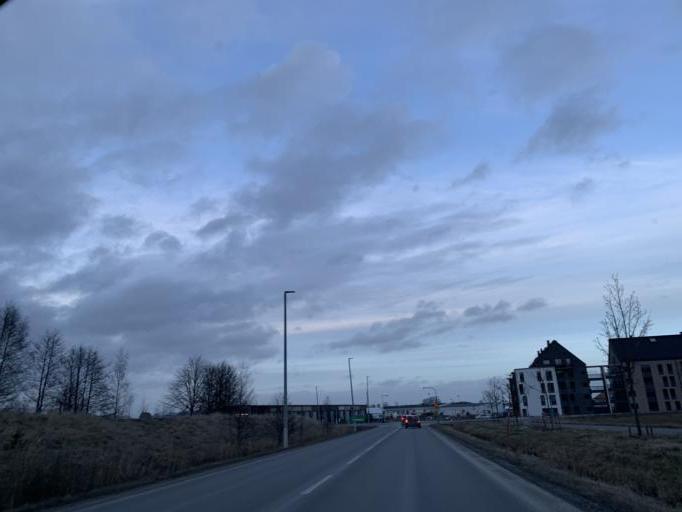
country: SE
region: OErebro
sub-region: Orebro Kommun
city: Orebro
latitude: 59.2577
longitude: 15.2606
